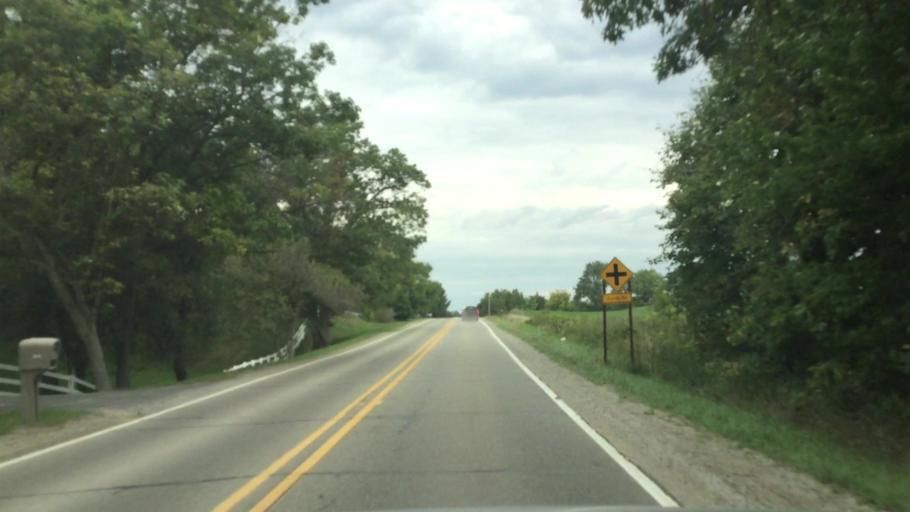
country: US
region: Michigan
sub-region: Livingston County
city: Howell
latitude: 42.6573
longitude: -83.8764
